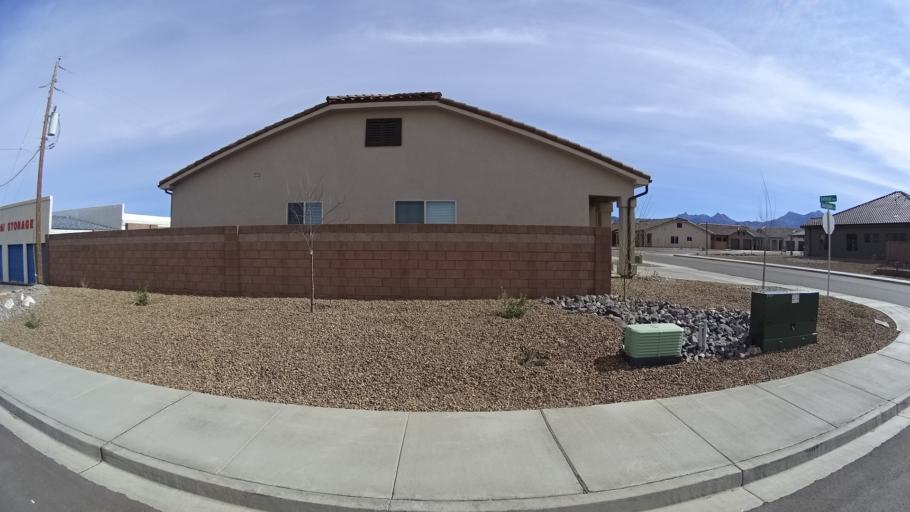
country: US
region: Arizona
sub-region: Mohave County
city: Kingman
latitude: 35.1906
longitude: -114.0202
